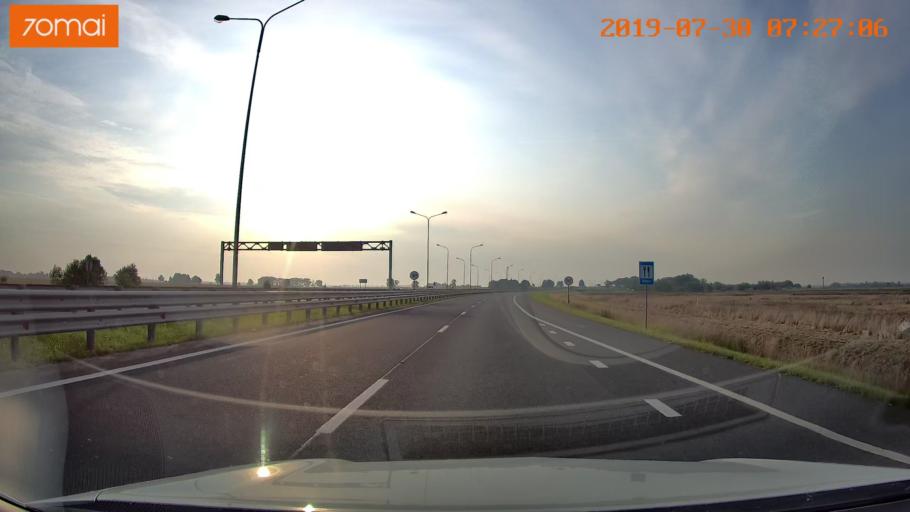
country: RU
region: Kaliningrad
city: Gvardeysk
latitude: 54.6835
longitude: 20.8786
